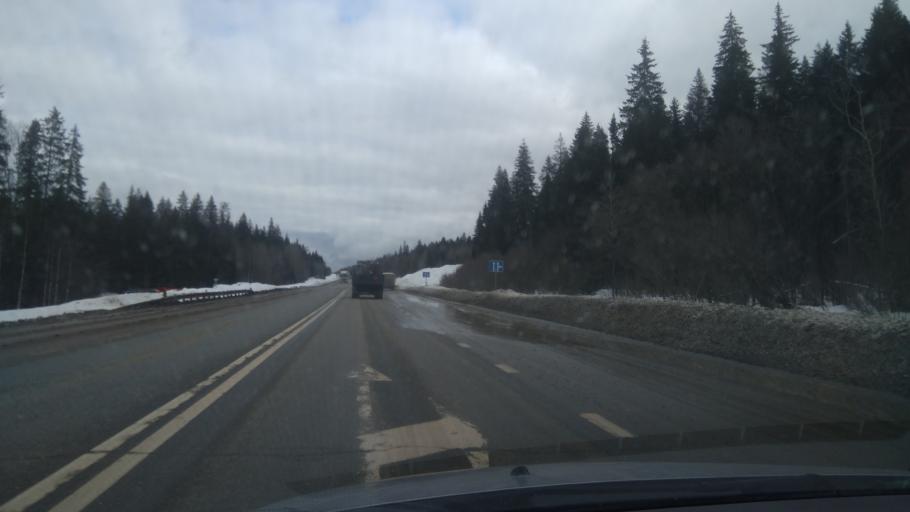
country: RU
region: Sverdlovsk
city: Bisert'
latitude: 56.8262
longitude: 59.2240
